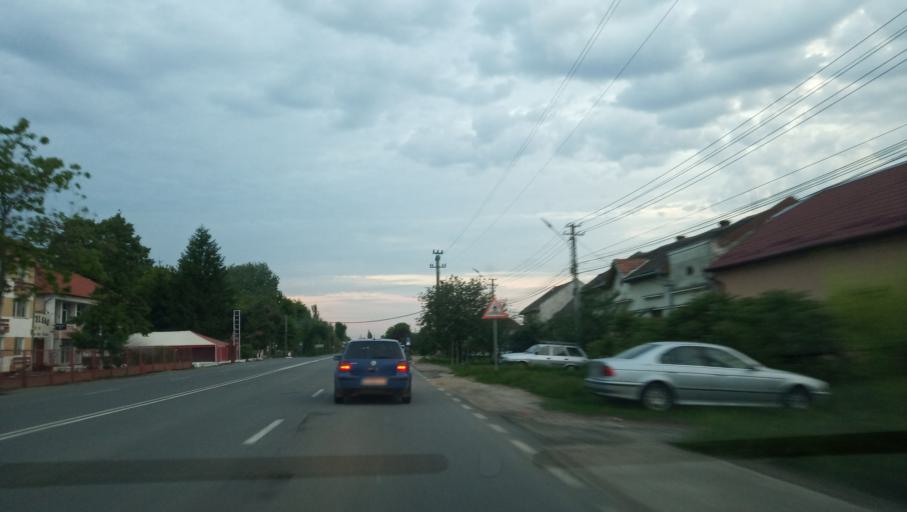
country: RO
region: Timis
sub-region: Comuna Sag
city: Sag
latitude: 45.6482
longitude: 21.1749
